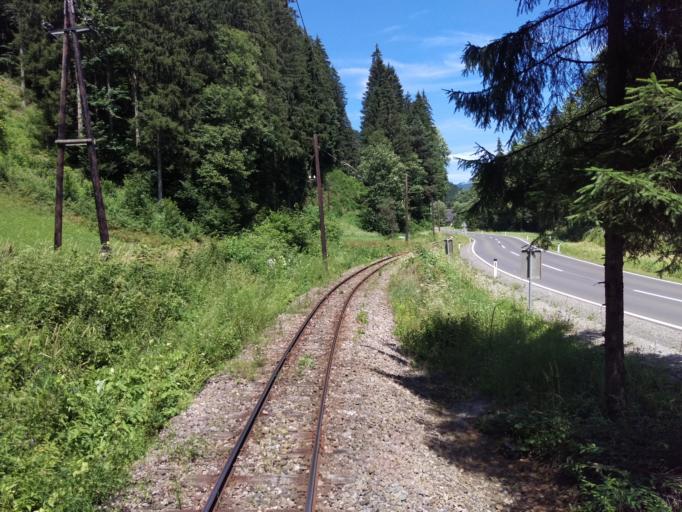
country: AT
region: Styria
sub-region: Politischer Bezirk Bruck-Muerzzuschlag
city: Pernegg an der Mur
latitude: 47.3769
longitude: 15.3970
